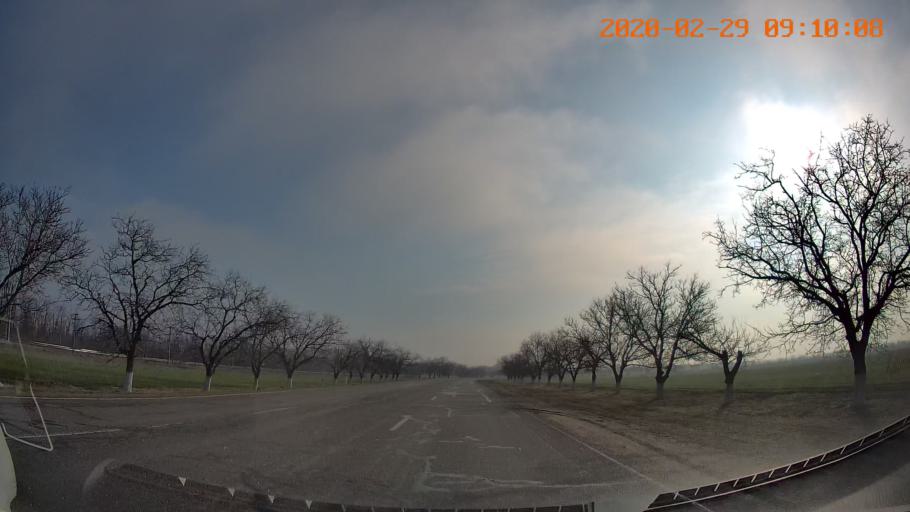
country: MD
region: Telenesti
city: Slobozia
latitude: 46.8449
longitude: 29.7762
